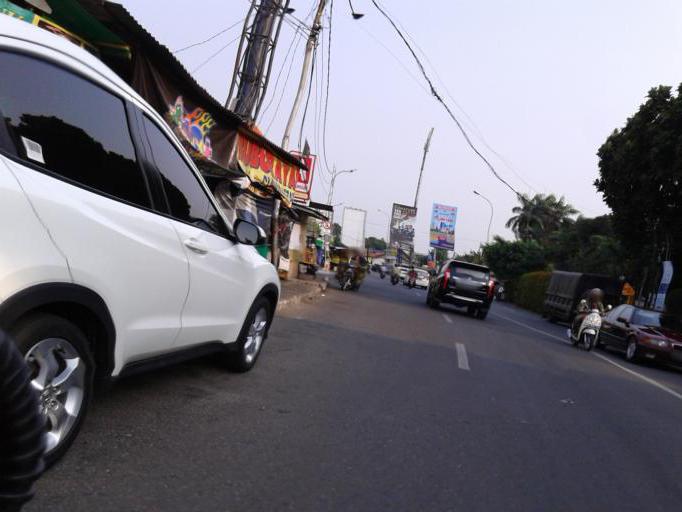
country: ID
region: Banten
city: South Tangerang
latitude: -6.2862
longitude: 106.7265
